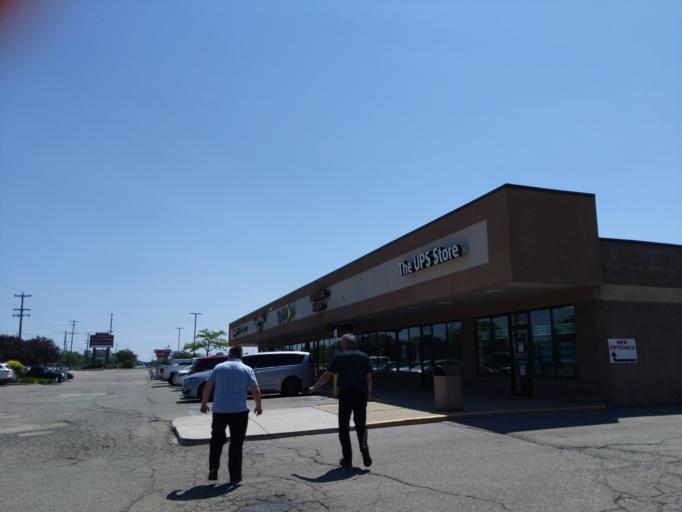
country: US
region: Michigan
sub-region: Eaton County
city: Waverly
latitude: 42.7407
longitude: -84.6347
